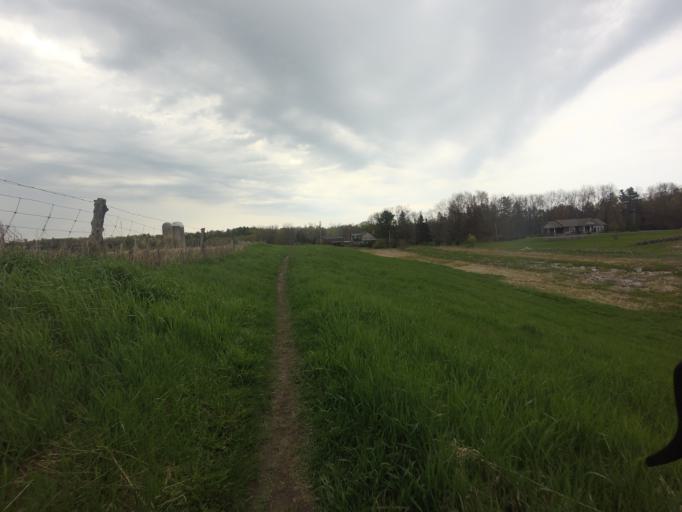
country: CA
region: Ontario
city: Carleton Place
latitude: 45.2277
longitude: -76.2085
